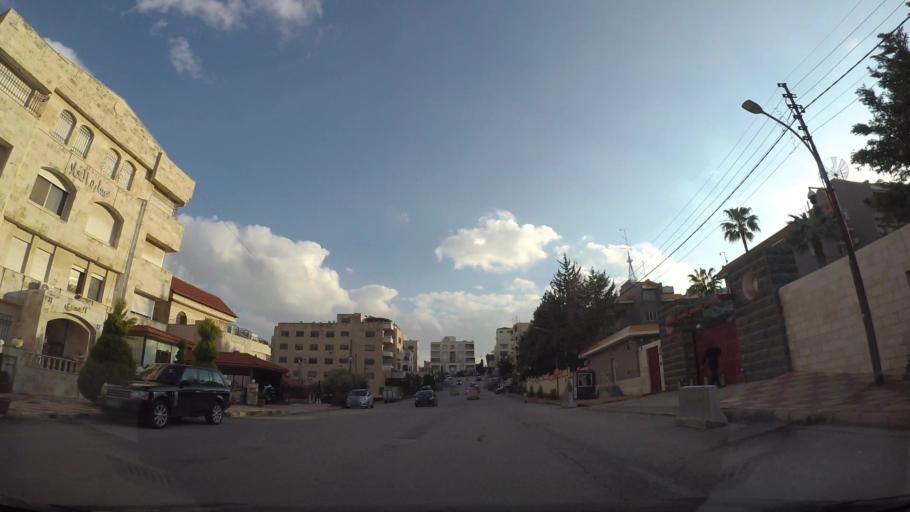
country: JO
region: Amman
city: Al Jubayhah
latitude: 31.9783
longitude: 35.8815
